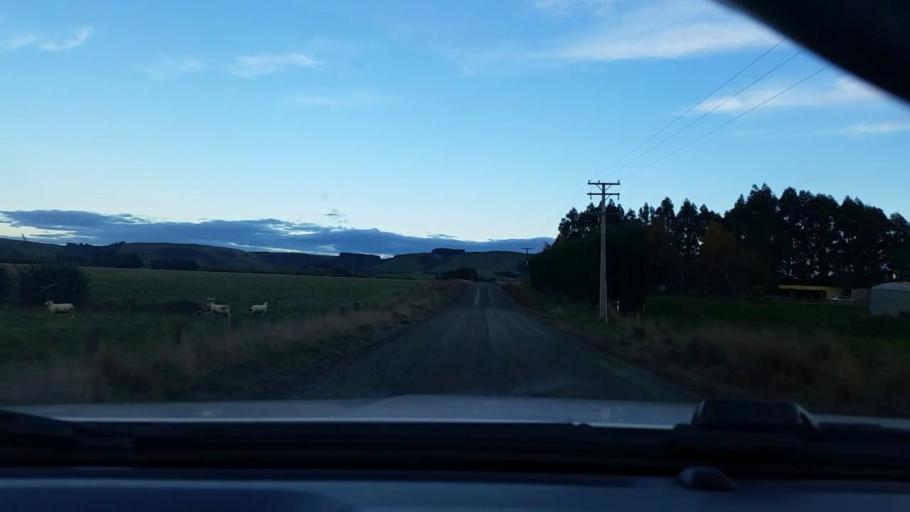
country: NZ
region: Southland
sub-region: Southland District
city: Winton
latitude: -46.1088
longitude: 168.4408
